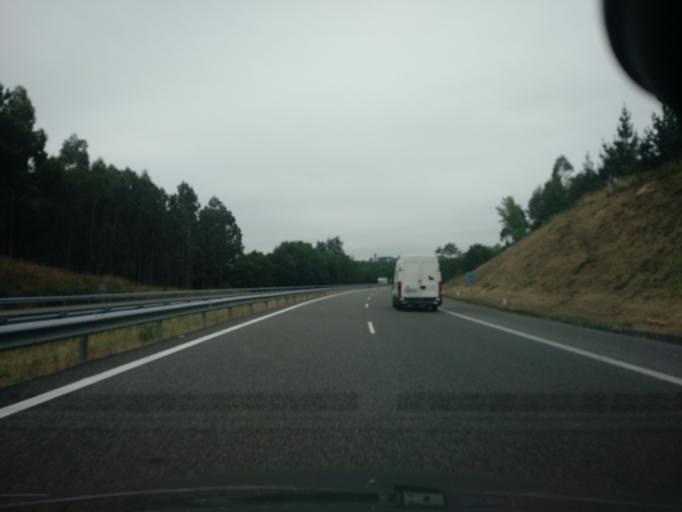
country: ES
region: Galicia
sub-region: Provincia da Coruna
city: Oroso
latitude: 43.0031
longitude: -8.4203
